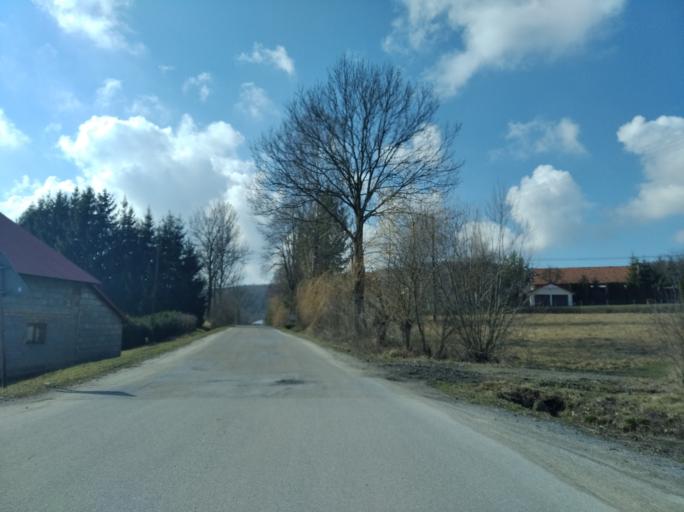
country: PL
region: Subcarpathian Voivodeship
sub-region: Powiat strzyzowski
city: Frysztak
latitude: 49.8737
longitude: 21.5665
